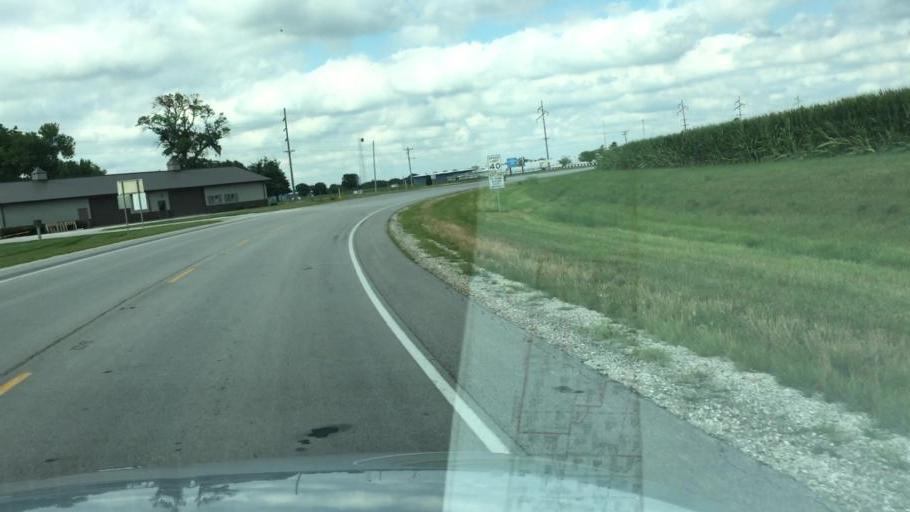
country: US
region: Illinois
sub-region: Hancock County
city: Carthage
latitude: 40.4155
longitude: -91.1542
